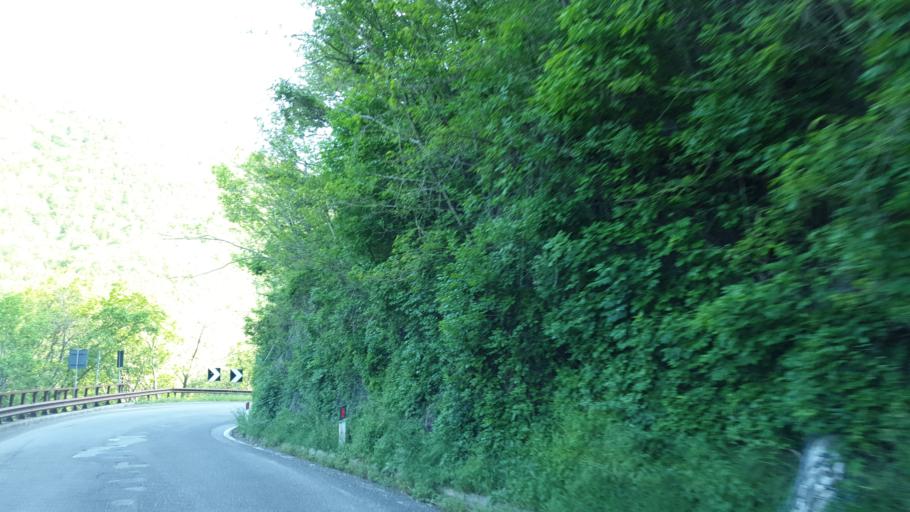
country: IT
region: Tuscany
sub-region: Province of Arezzo
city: Soci
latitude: 43.7738
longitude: 11.8674
